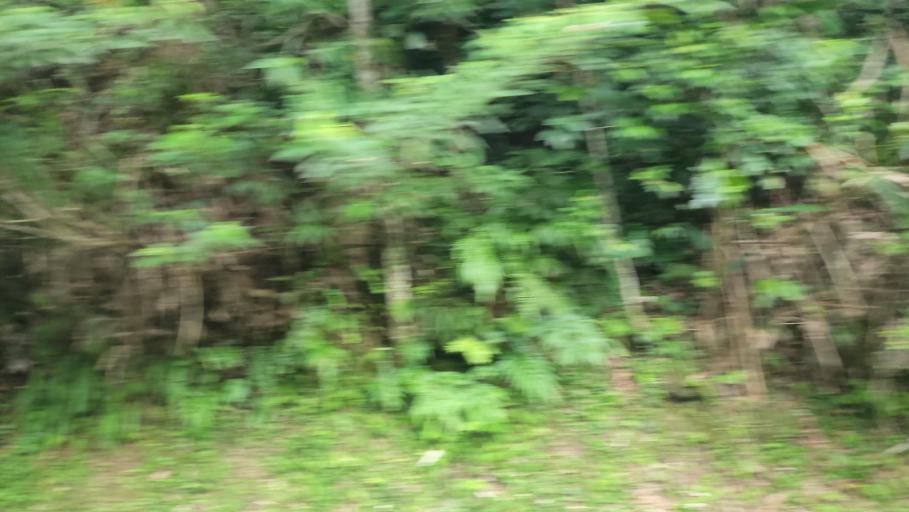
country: TW
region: Taipei
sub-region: Taipei
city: Banqiao
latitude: 24.8924
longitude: 121.4284
